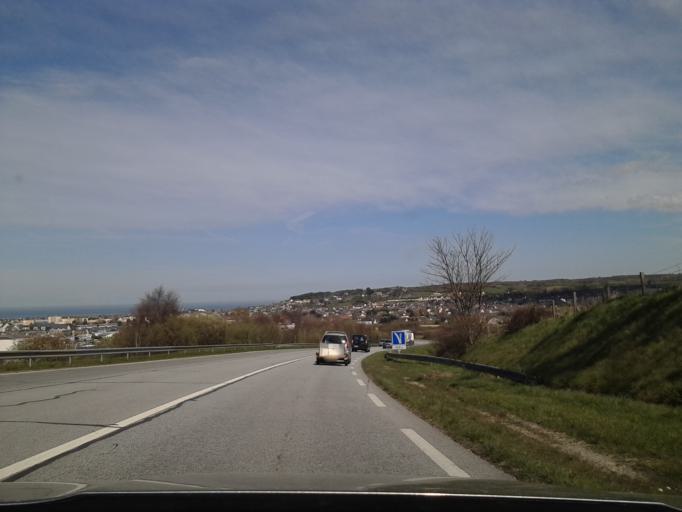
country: FR
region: Lower Normandy
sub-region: Departement de la Manche
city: Tourlaville
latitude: 49.6288
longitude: -1.5815
